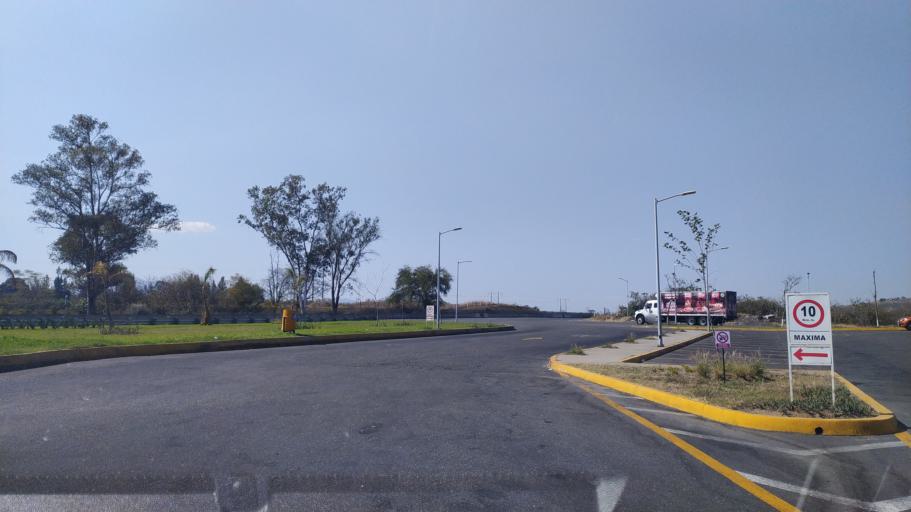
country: MX
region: Jalisco
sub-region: Zapotlan el Grande
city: Ciudad Guzman [CERESO]
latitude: 19.6300
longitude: -103.4651
